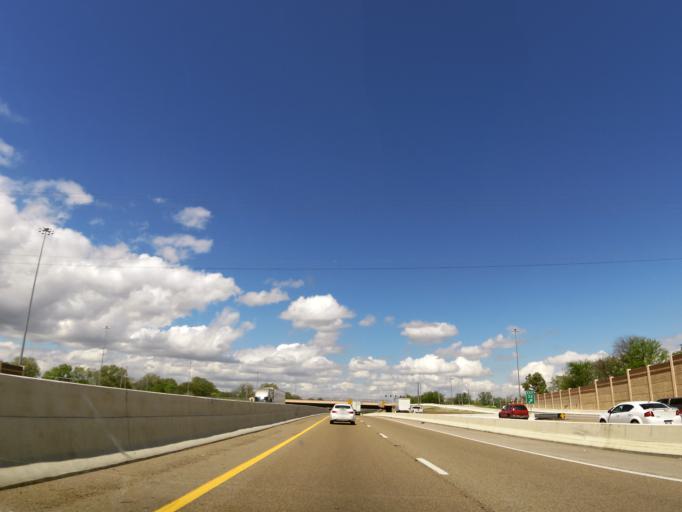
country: US
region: Tennessee
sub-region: Shelby County
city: Memphis
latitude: 35.1555
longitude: -90.0209
